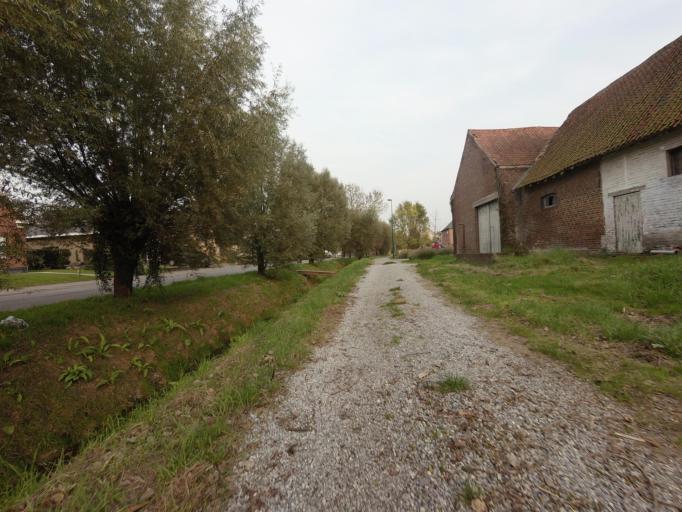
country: BE
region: Flanders
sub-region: Provincie Vlaams-Brabant
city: Grimbergen
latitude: 50.9334
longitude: 4.3598
